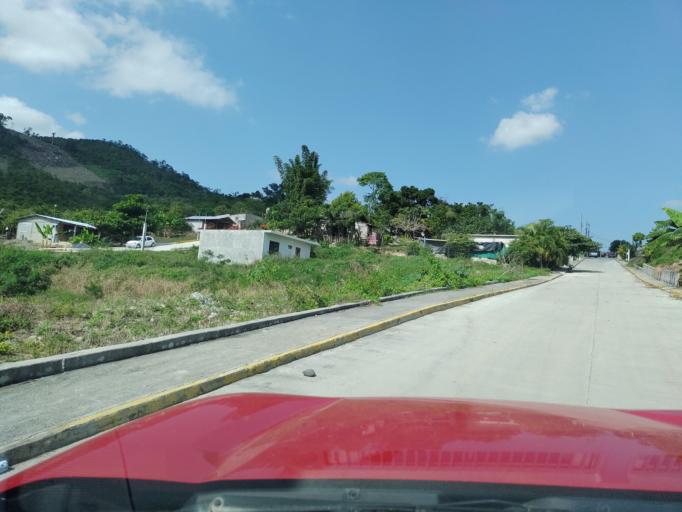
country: MX
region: Veracruz
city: Agua Dulce
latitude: 20.3035
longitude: -97.1729
